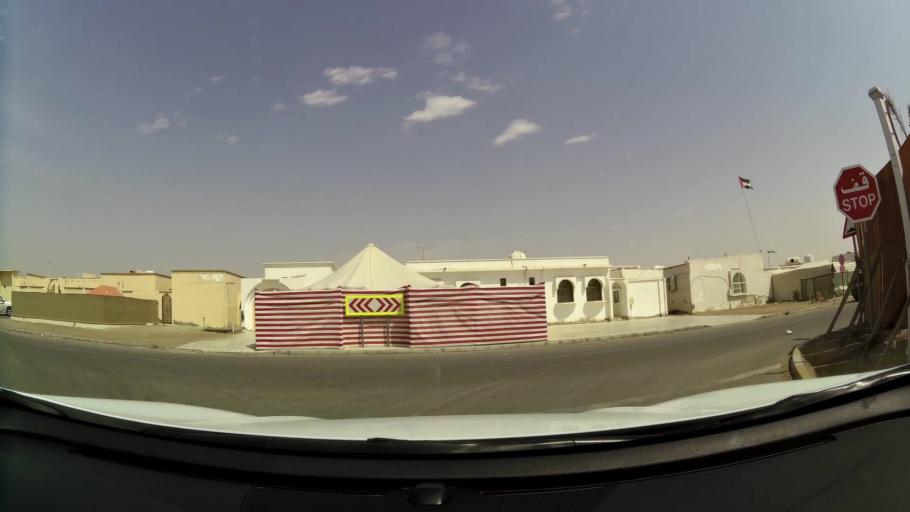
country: AE
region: Abu Dhabi
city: Abu Dhabi
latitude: 24.2937
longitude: 54.6491
